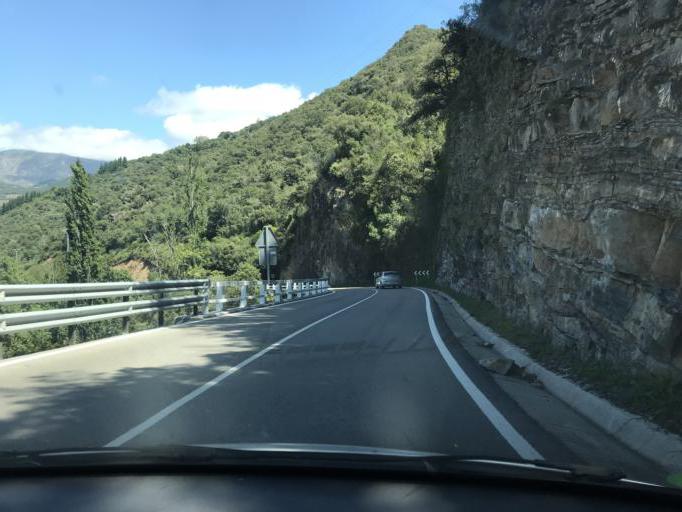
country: ES
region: Cantabria
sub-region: Provincia de Cantabria
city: Cabezon de Liebana
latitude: 43.1113
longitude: -4.5729
